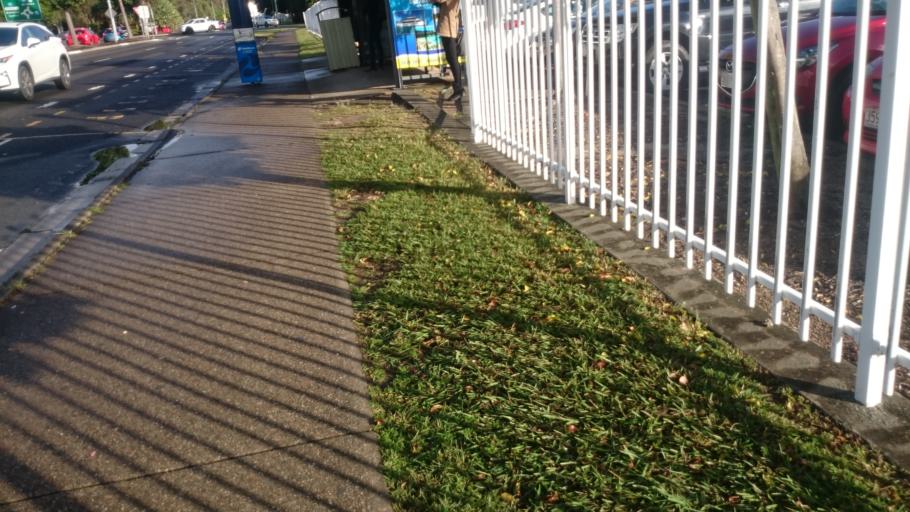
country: AU
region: Queensland
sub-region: Redland
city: Cleveland
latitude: -27.5245
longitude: 153.2658
